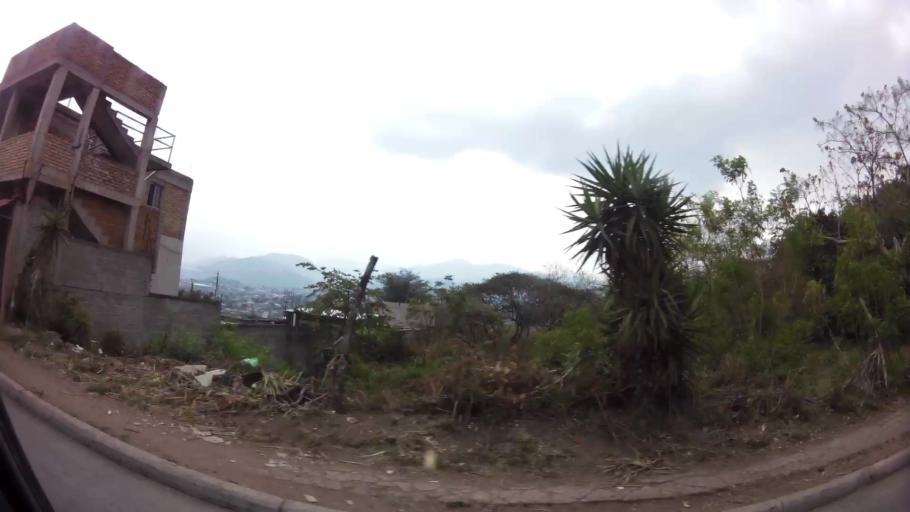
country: HN
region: Francisco Morazan
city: Tegucigalpa
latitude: 14.0966
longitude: -87.1715
